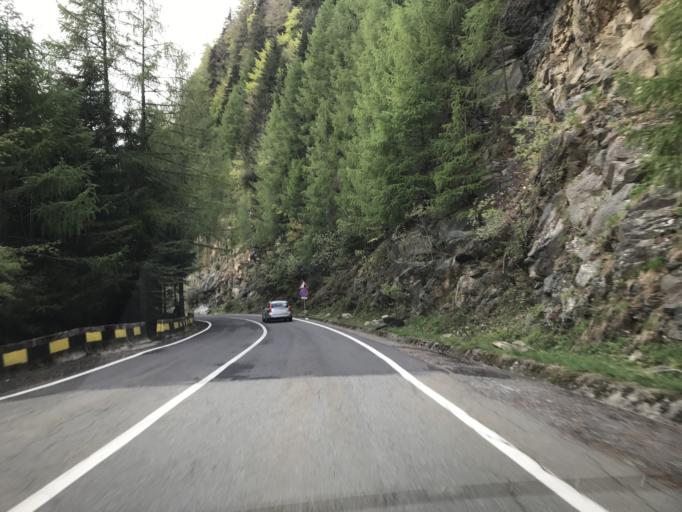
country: RO
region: Sibiu
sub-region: Comuna Cartisoara
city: Cartisoara
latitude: 45.6580
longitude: 24.6001
